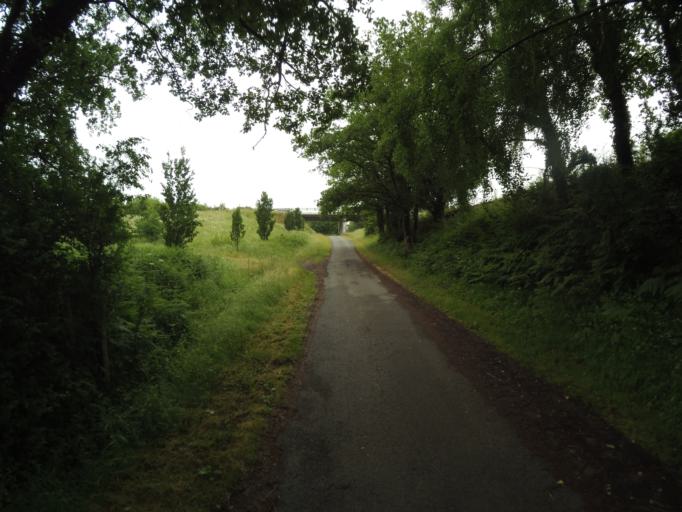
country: FR
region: Pays de la Loire
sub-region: Departement de la Vendee
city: Nesmy
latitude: 46.6262
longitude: -1.4218
